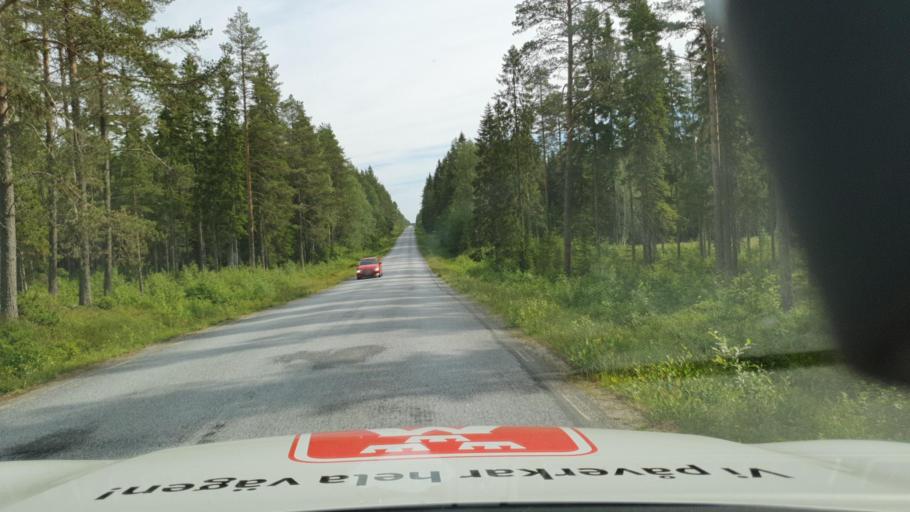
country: SE
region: Vaesterbotten
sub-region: Umea Kommun
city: Saevar
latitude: 63.8802
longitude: 20.7123
